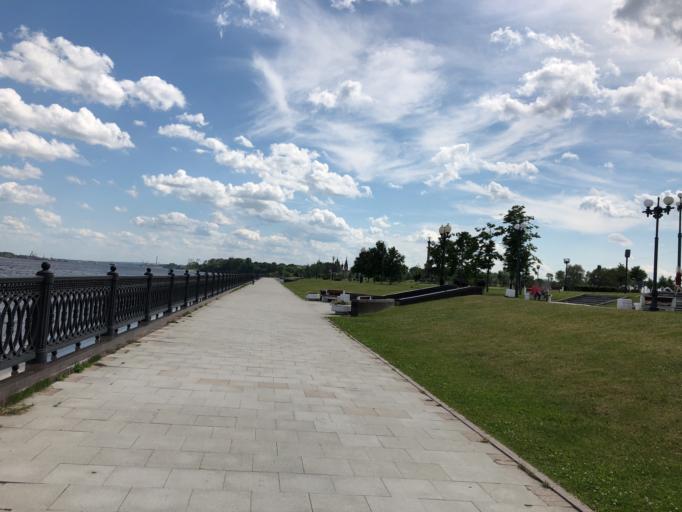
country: RU
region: Jaroslavl
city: Yaroslavl
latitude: 57.6200
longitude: 39.9053
